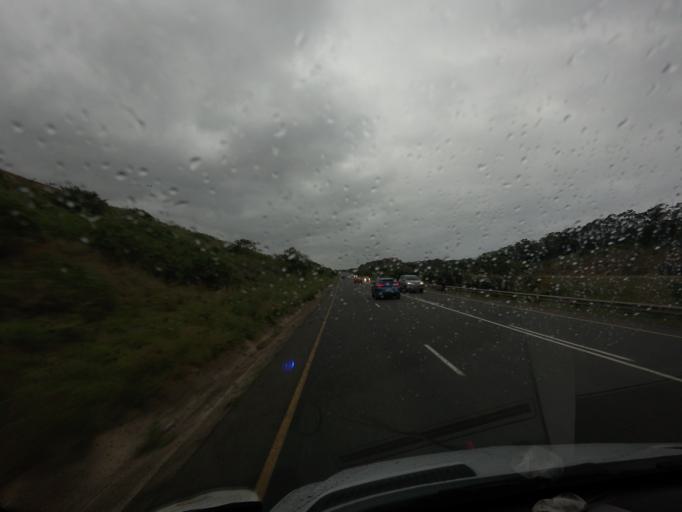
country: ZA
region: KwaZulu-Natal
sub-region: iLembe District Municipality
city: Ballitoville
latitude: -29.5531
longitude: 31.1837
